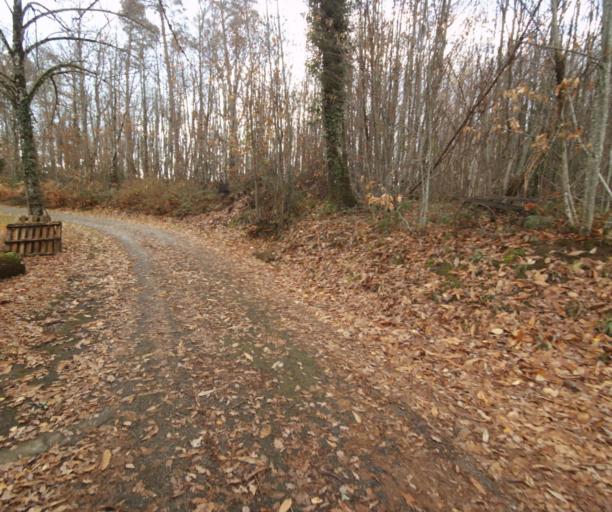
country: FR
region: Limousin
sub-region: Departement de la Correze
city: Sainte-Fortunade
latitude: 45.2211
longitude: 1.7904
